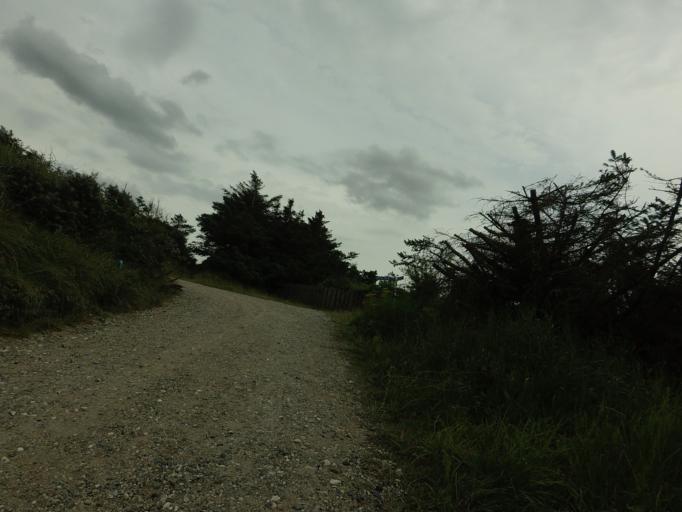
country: DK
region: North Denmark
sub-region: Jammerbugt Kommune
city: Pandrup
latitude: 57.3042
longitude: 9.6464
